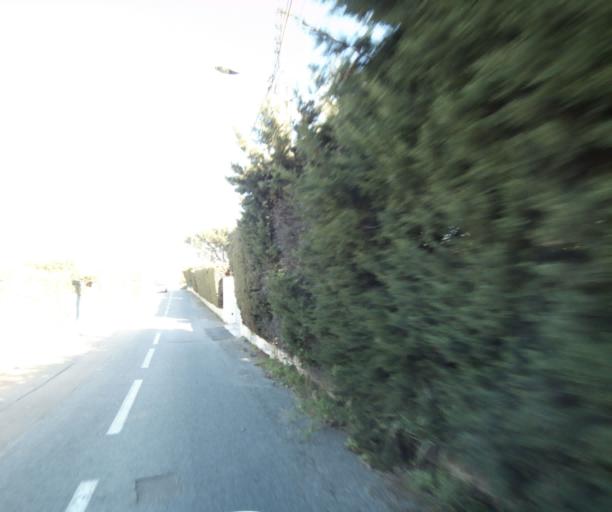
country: FR
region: Provence-Alpes-Cote d'Azur
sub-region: Departement des Alpes-Maritimes
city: Biot
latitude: 43.6097
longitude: 7.0942
